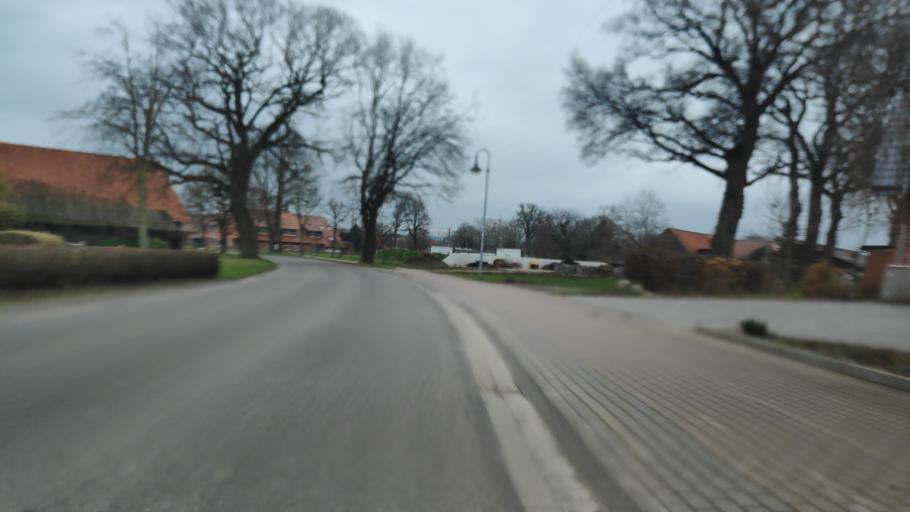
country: DE
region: North Rhine-Westphalia
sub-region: Regierungsbezirk Detmold
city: Hille
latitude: 52.3163
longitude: 8.8173
